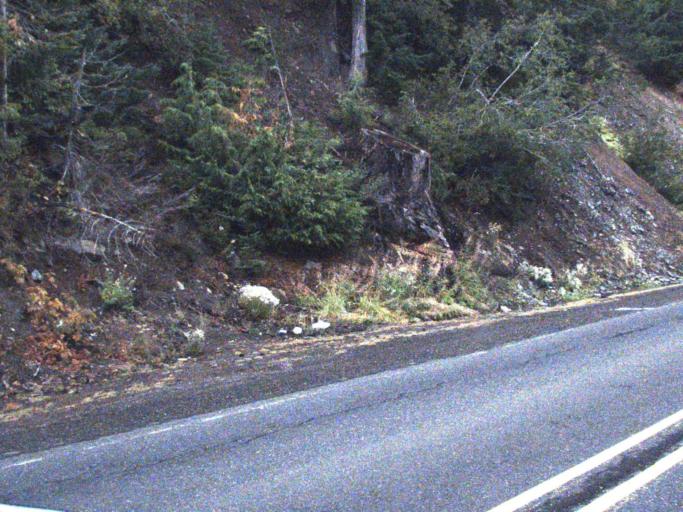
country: US
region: Washington
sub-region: Yakima County
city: Tieton
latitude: 46.6284
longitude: -121.4205
